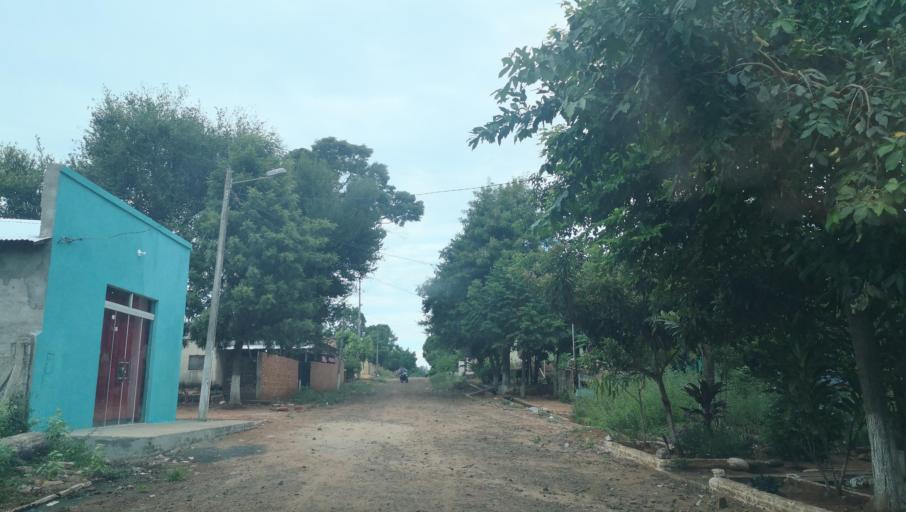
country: PY
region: San Pedro
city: Capiibary
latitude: -24.7319
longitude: -56.0220
